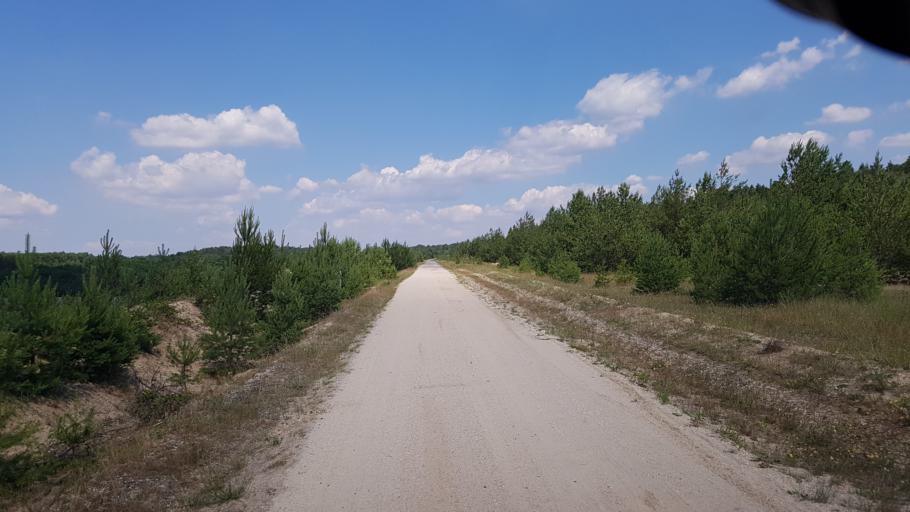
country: DE
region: Brandenburg
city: Sallgast
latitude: 51.5813
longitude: 13.7999
